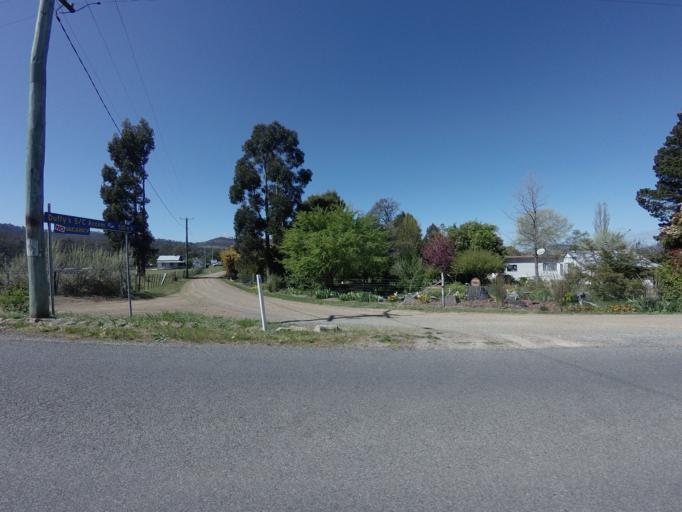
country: AU
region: Tasmania
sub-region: Derwent Valley
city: New Norfolk
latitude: -42.6696
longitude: 146.7903
